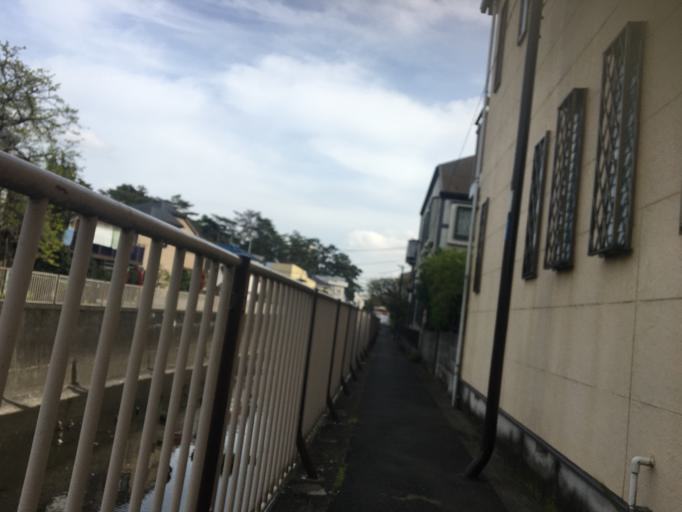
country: JP
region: Tokyo
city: Musashino
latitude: 35.6997
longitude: 139.6197
